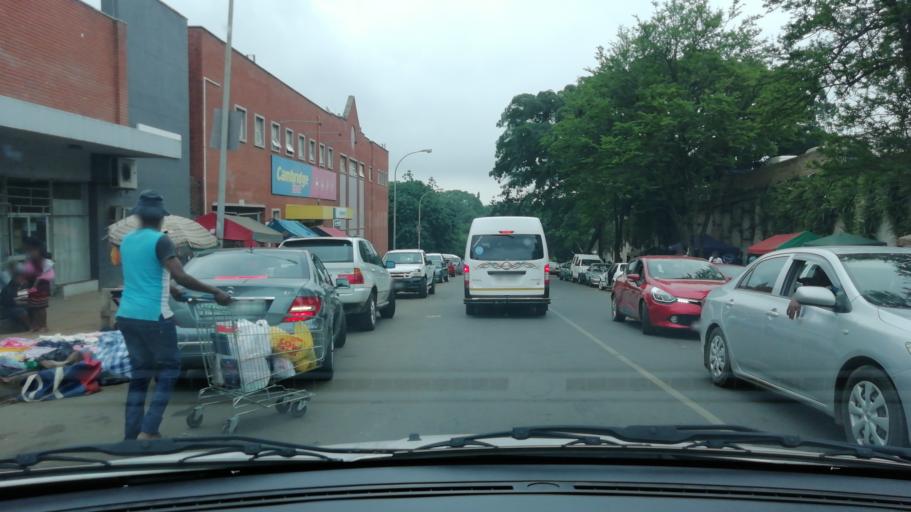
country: ZA
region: KwaZulu-Natal
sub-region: uThungulu District Municipality
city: Empangeni
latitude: -28.7441
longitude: 31.8874
